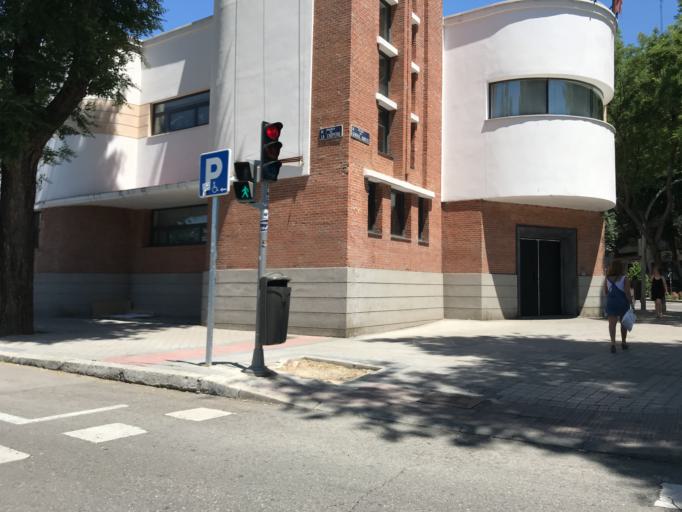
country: ES
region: Madrid
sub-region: Provincia de Madrid
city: Usera
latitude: 40.3938
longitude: -3.6988
